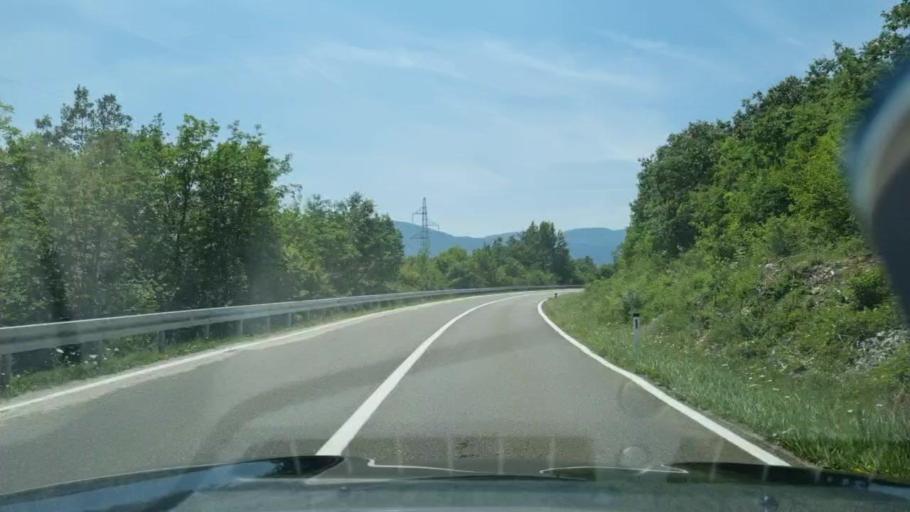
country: BA
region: Federation of Bosnia and Herzegovina
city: Sanica
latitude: 44.5499
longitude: 16.4345
